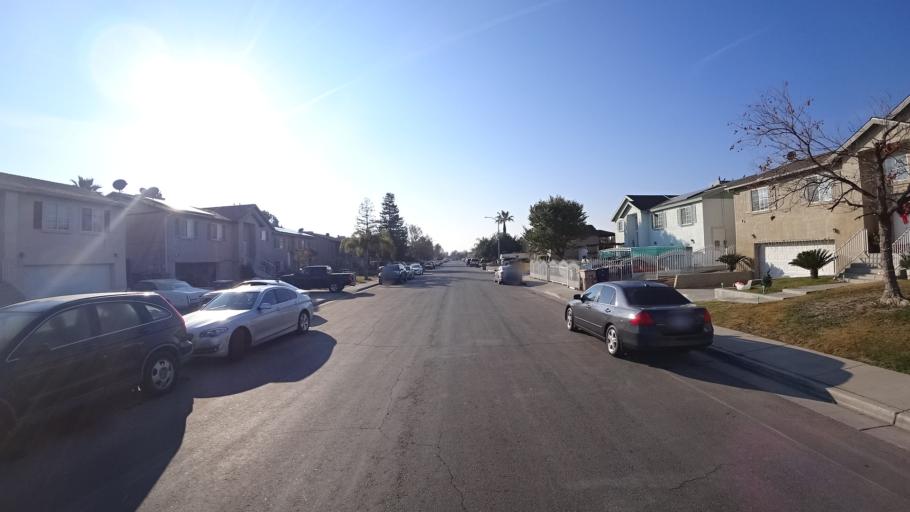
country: US
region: California
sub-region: Kern County
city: Greenfield
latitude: 35.3090
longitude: -119.0113
